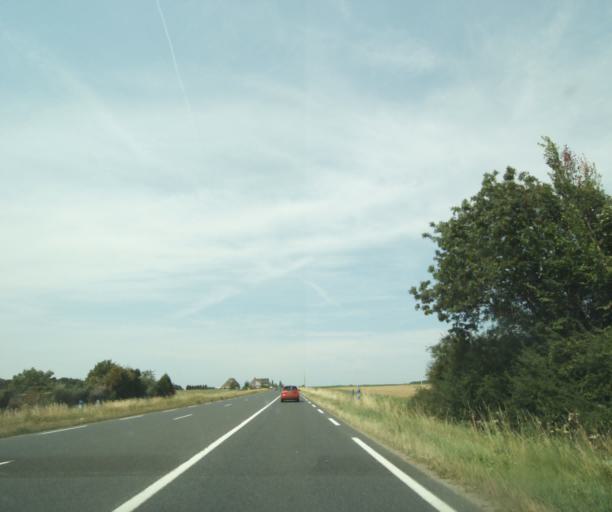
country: FR
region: Centre
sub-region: Departement d'Indre-et-Loire
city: Sorigny
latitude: 47.1919
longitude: 0.6659
